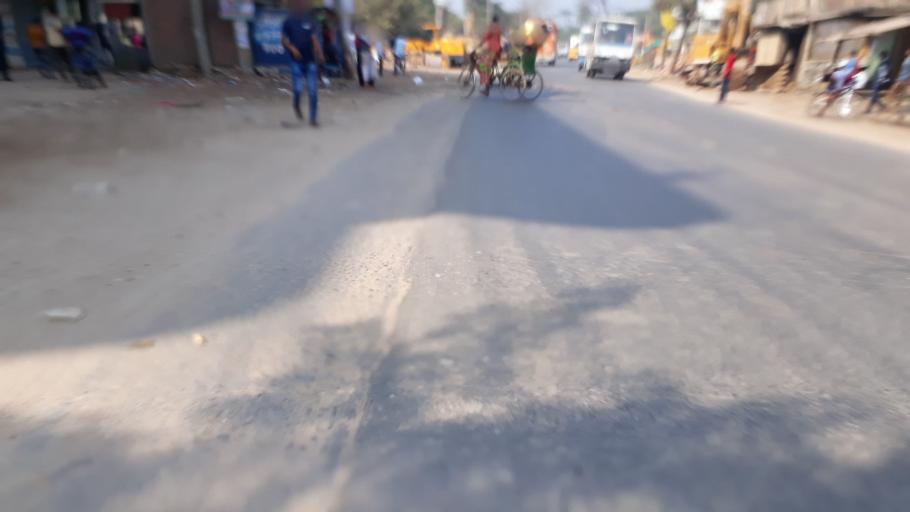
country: BD
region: Dhaka
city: Tungi
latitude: 23.9004
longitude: 90.3272
